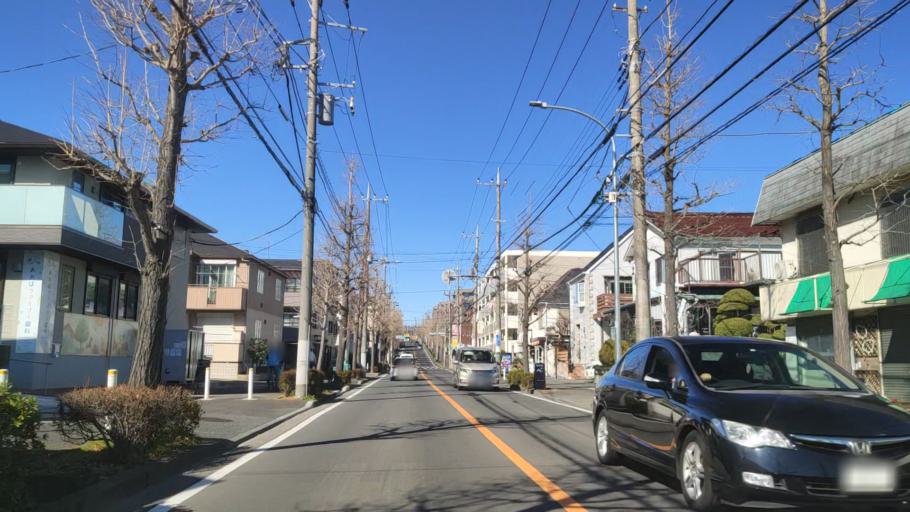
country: JP
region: Tokyo
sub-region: Machida-shi
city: Machida
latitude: 35.5493
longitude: 139.5082
